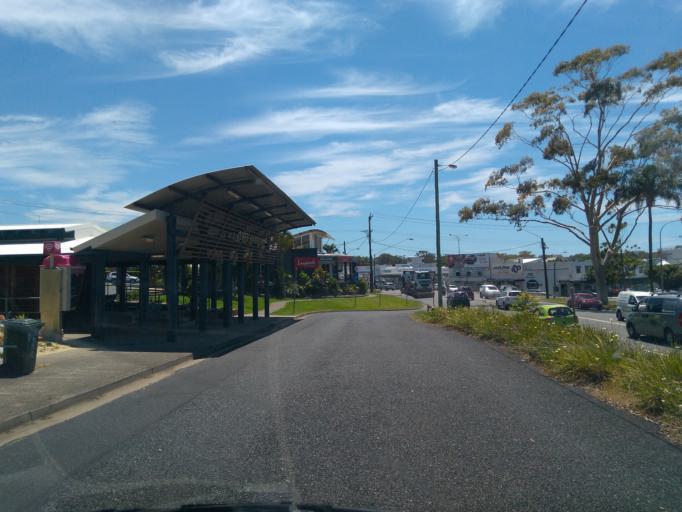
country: AU
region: New South Wales
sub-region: Coffs Harbour
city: Coffs Harbour
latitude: -30.2992
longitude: 153.1117
